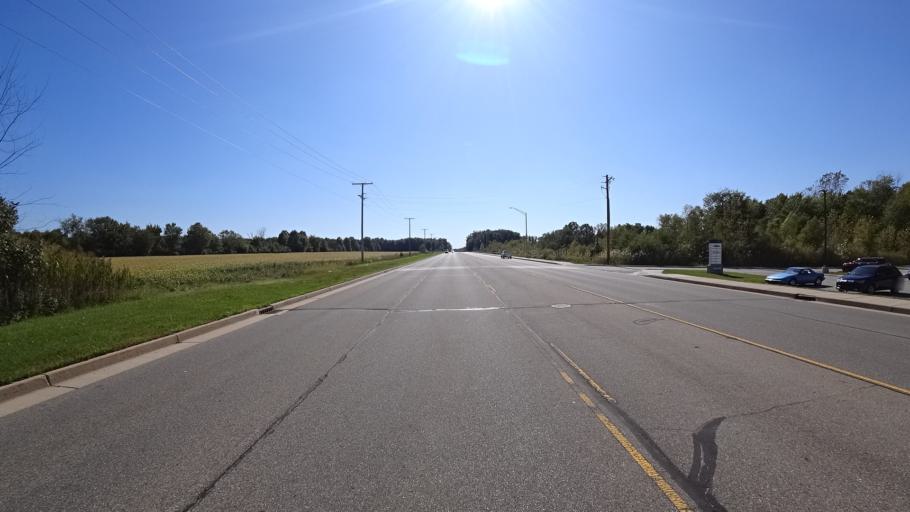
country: US
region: Indiana
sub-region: LaPorte County
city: Michigan City
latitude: 41.6779
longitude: -86.8844
